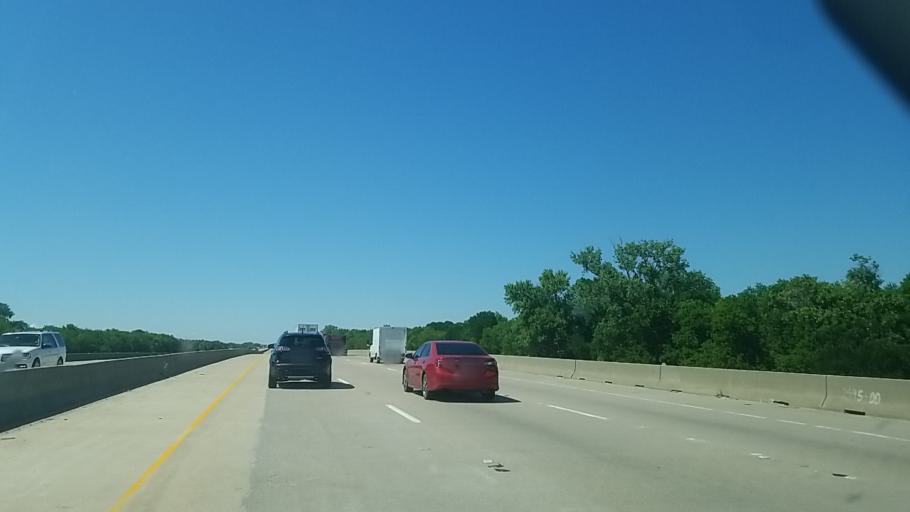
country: US
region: Texas
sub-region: Navarro County
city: Corsicana
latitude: 32.1564
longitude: -96.4683
